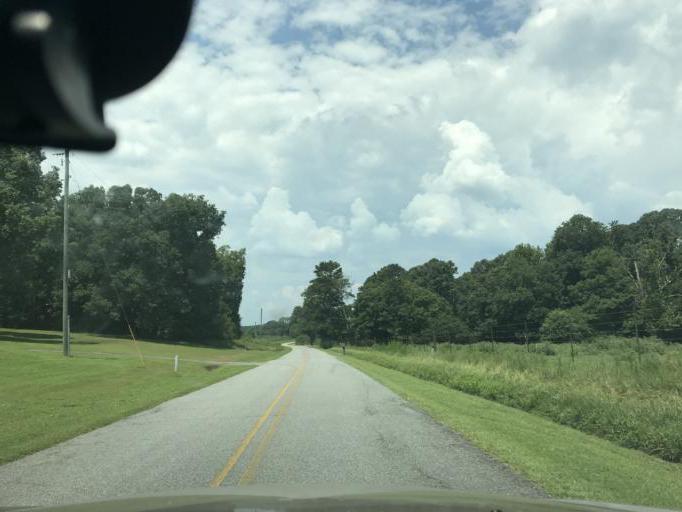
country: US
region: Georgia
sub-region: Dawson County
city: Dawsonville
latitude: 34.3321
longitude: -84.1268
